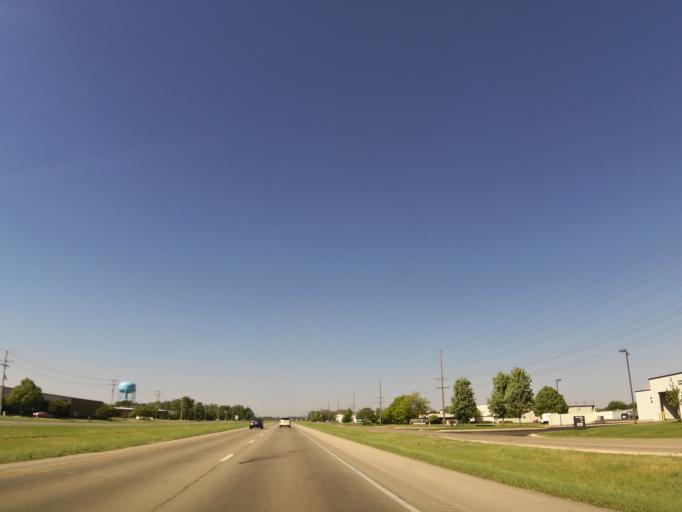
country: US
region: Illinois
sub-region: Winnebago County
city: Machesney Park
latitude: 42.3736
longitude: -89.0289
